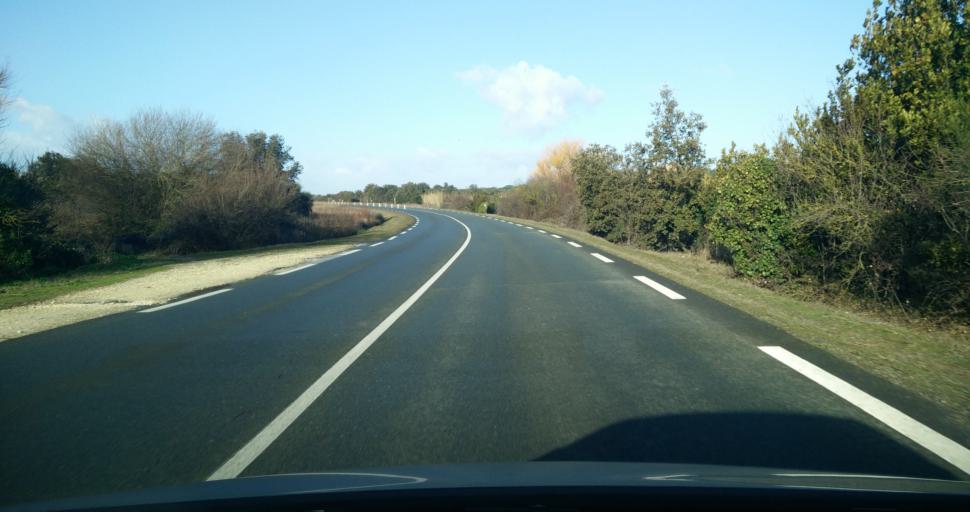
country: FR
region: Poitou-Charentes
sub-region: Departement de la Charente-Maritime
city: Rivedoux-Plage
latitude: 46.1520
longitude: -1.2791
